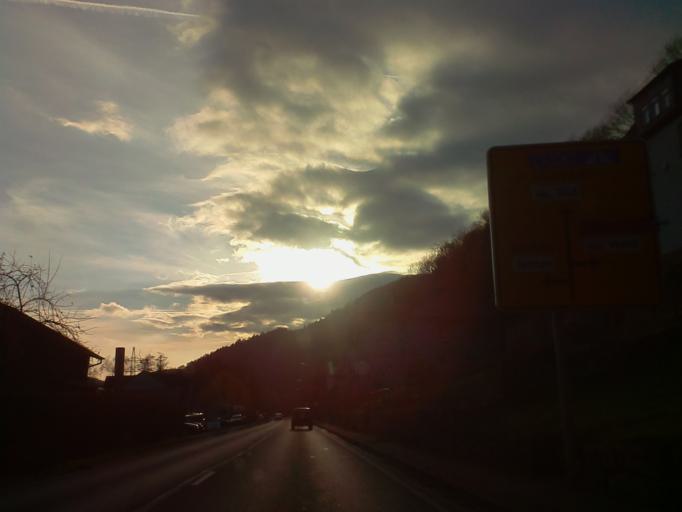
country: DE
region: Bavaria
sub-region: Regierungsbezirk Unterfranken
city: Weilbach
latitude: 49.6721
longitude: 9.2148
